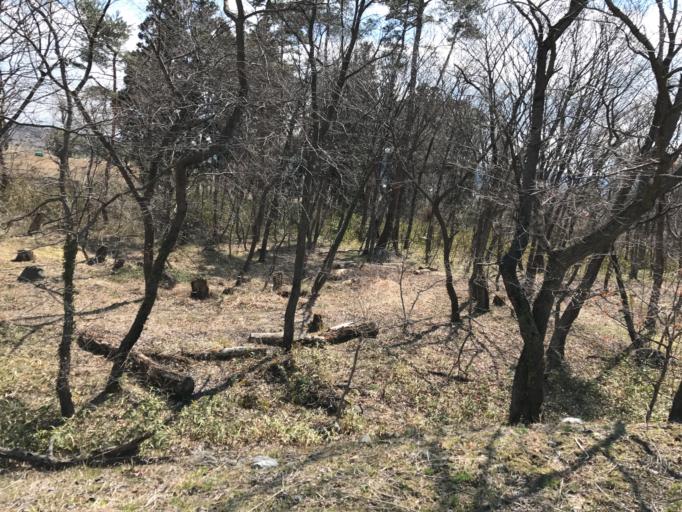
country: JP
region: Fukushima
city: Fukushima-shi
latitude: 37.7323
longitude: 140.3825
